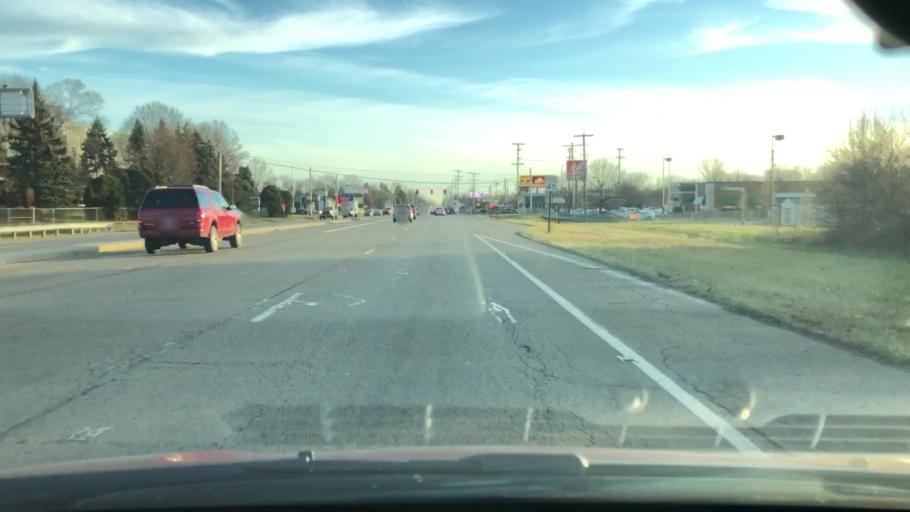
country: US
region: Ohio
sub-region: Franklin County
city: Minerva Park
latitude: 40.1024
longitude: -82.9499
